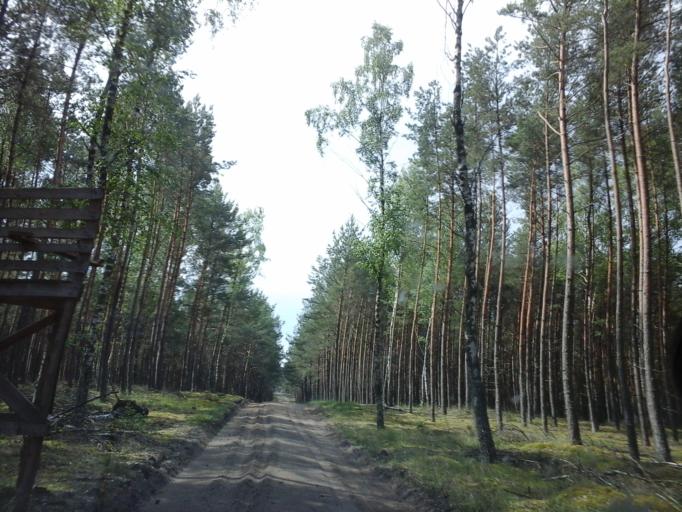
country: PL
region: West Pomeranian Voivodeship
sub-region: Powiat choszczenski
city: Drawno
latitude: 53.1806
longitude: 15.7606
